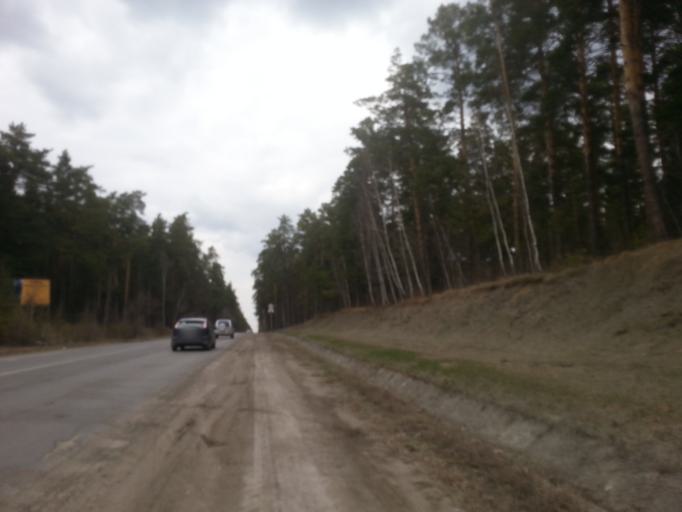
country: RU
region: Altai Krai
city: Yuzhnyy
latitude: 53.2707
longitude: 83.7246
